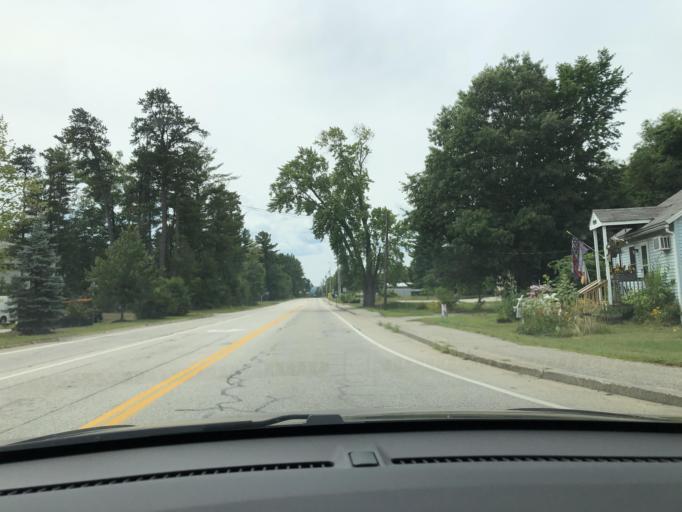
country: US
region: New Hampshire
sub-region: Merrimack County
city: Concord
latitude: 43.2064
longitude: -71.5108
